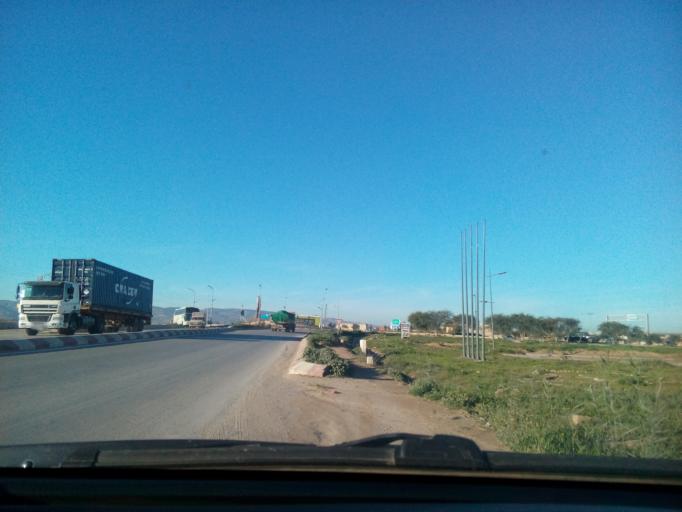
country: DZ
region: Relizane
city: Relizane
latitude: 35.7857
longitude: 0.5286
